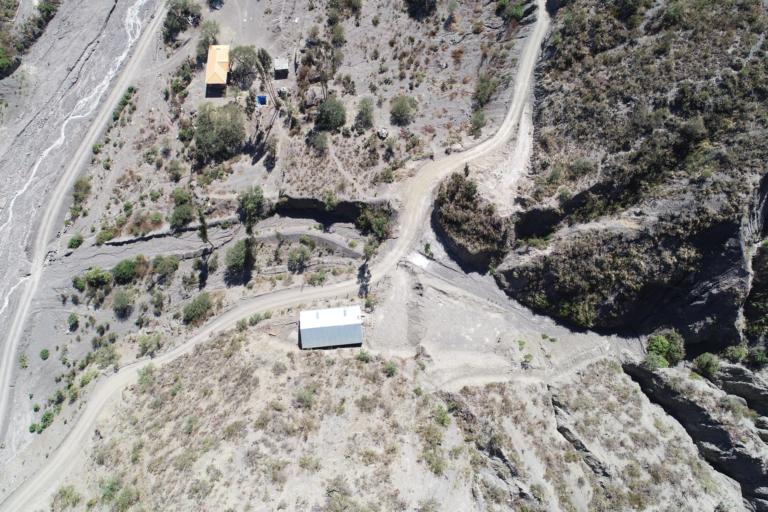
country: BO
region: La Paz
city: La Paz
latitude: -16.6268
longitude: -68.0408
